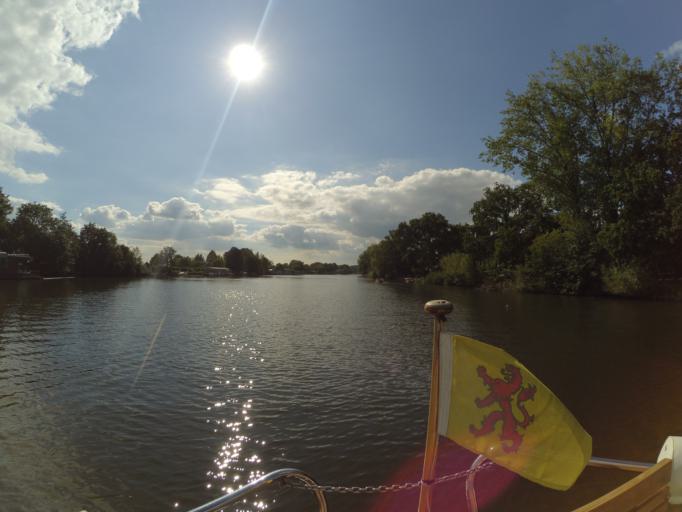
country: NL
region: Utrecht
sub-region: Stichtse Vecht
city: Vreeland
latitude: 52.2009
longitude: 5.0194
